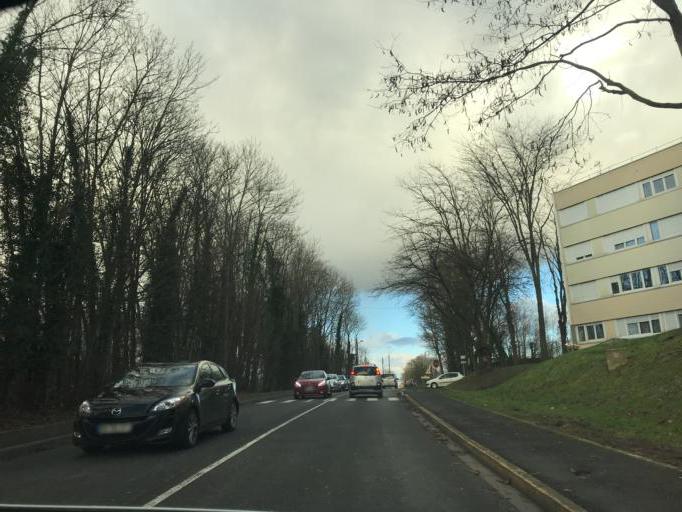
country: FR
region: Ile-de-France
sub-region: Departement de Seine-et-Marne
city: Claye-Souilly
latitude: 48.9471
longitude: 2.6906
